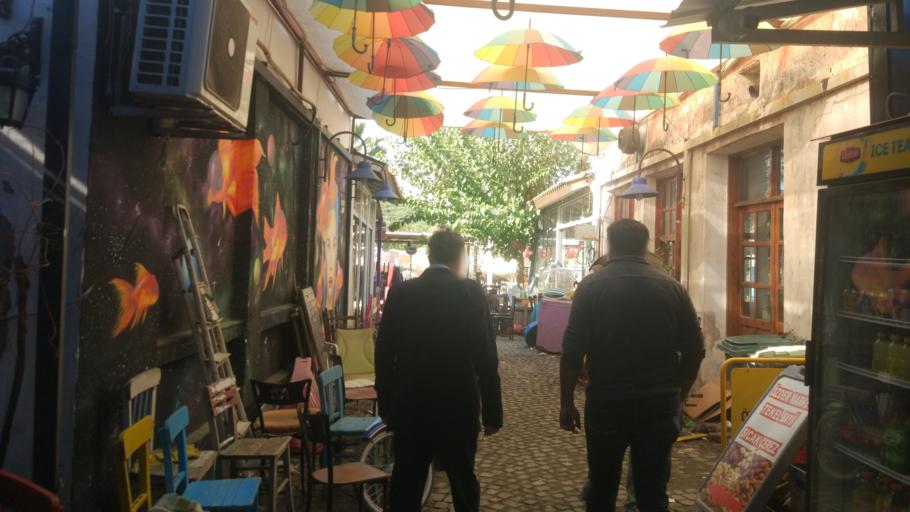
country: TR
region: Izmir
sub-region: Seferihisar
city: Seferhisar
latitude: 38.1936
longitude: 26.7847
